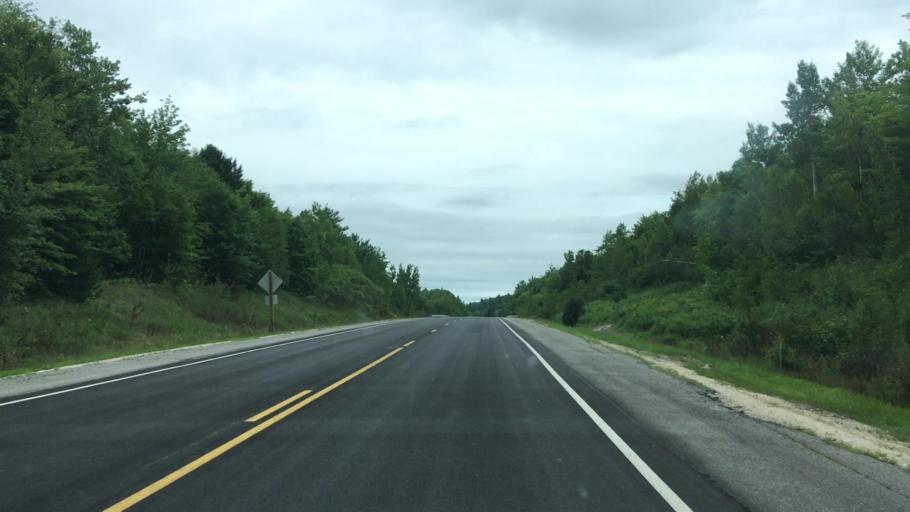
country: US
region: Maine
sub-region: Washington County
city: Cherryfield
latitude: 44.8875
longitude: -67.8567
